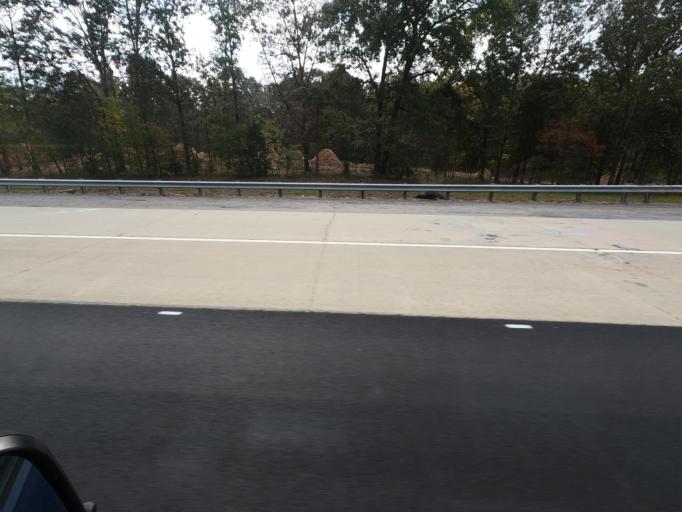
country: US
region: Tennessee
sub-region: Dickson County
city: Burns
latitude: 36.0246
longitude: -87.2831
